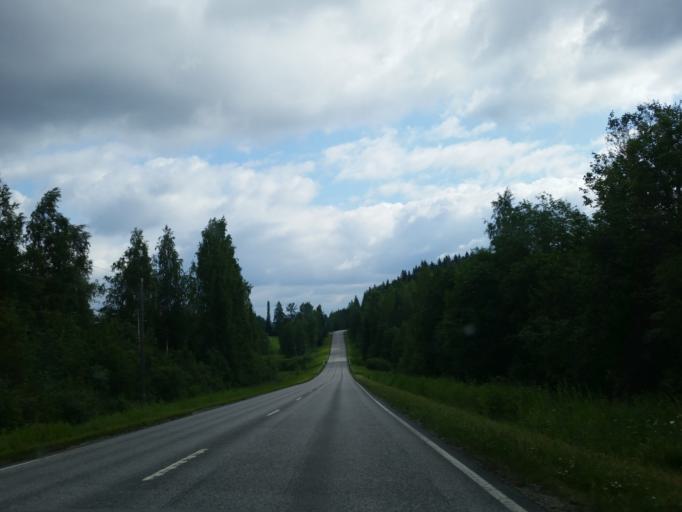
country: FI
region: Northern Savo
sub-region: Kuopio
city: Kuopio
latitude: 62.8454
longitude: 27.5227
